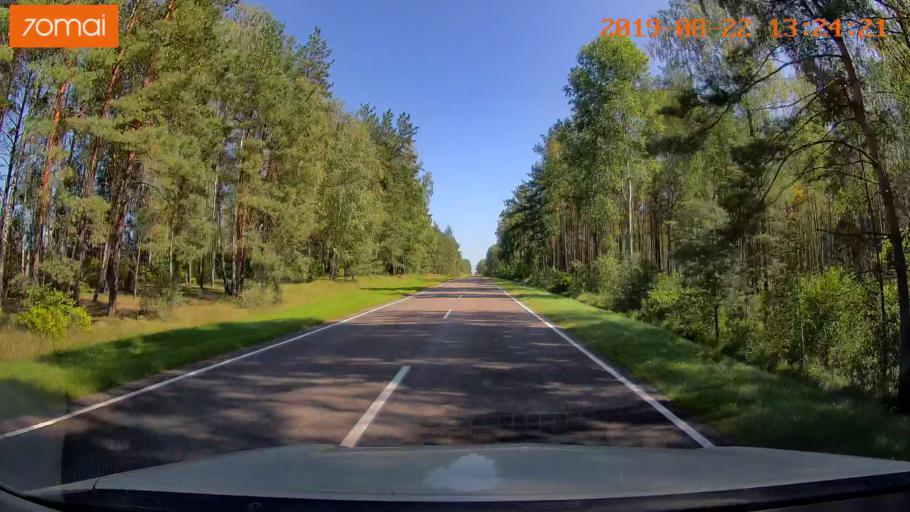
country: BY
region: Minsk
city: Urechcha
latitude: 53.2109
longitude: 28.0191
